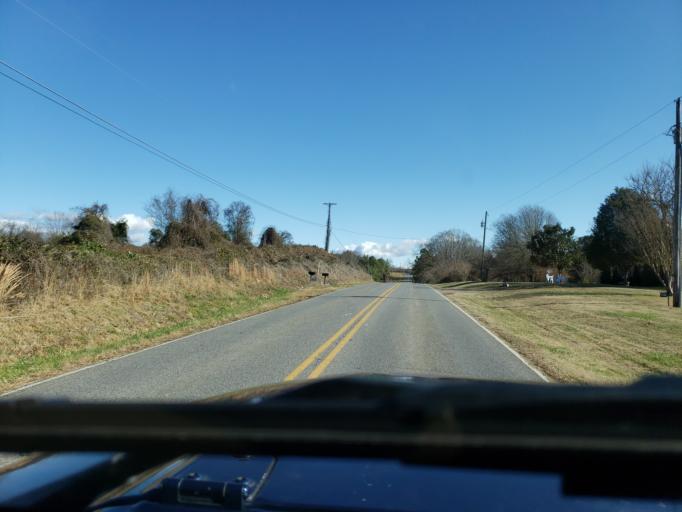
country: US
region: South Carolina
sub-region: Cherokee County
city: Blacksburg
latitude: 35.1922
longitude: -81.4771
